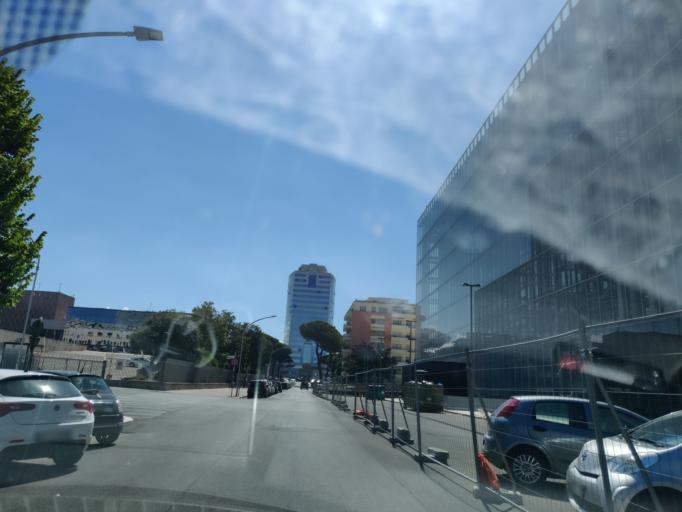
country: IT
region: Latium
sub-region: Citta metropolitana di Roma Capitale
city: Selcetta
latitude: 41.8315
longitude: 12.4718
